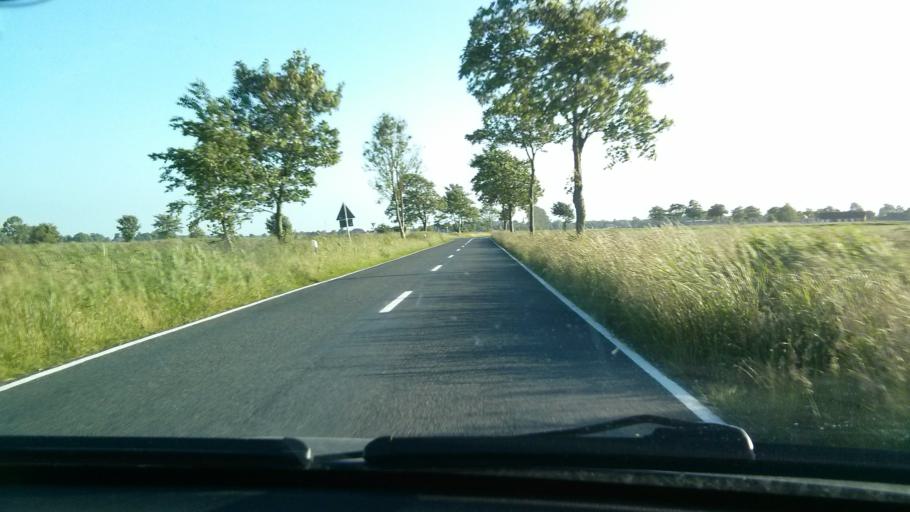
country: DE
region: Lower Saxony
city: Nordenham
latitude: 53.4578
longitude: 8.5180
